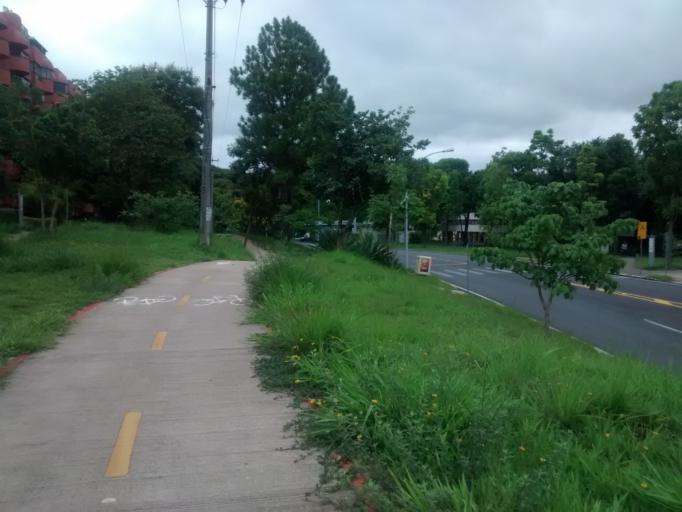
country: BR
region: Federal District
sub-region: Brasilia
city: Brasilia
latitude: -15.7414
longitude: -47.8873
